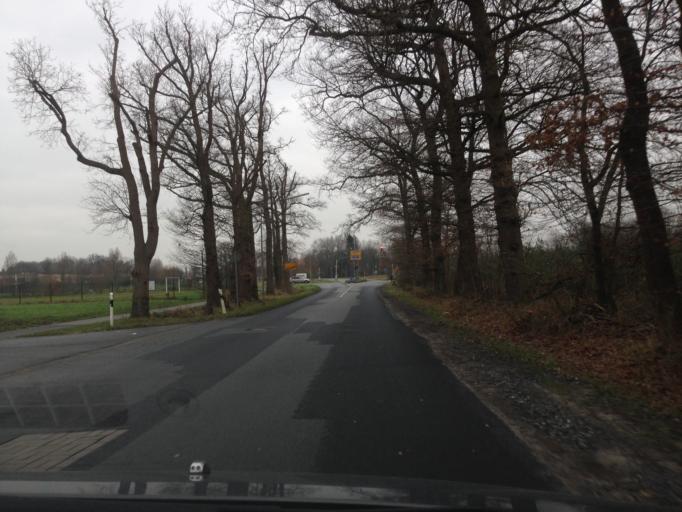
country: DE
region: Lower Saxony
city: Bad Bentheim
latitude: 52.2967
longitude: 7.1361
